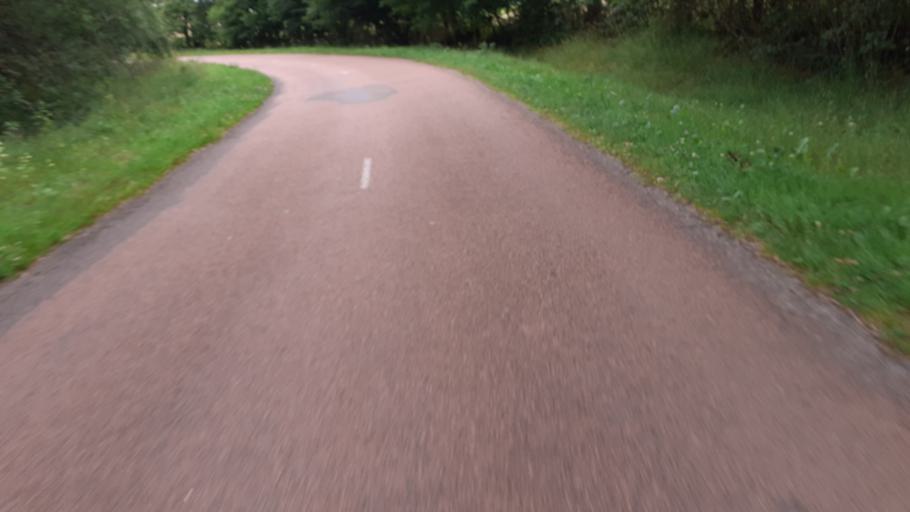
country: FR
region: Bourgogne
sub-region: Departement de la Cote-d'Or
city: Saulieu
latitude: 47.2825
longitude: 4.1423
